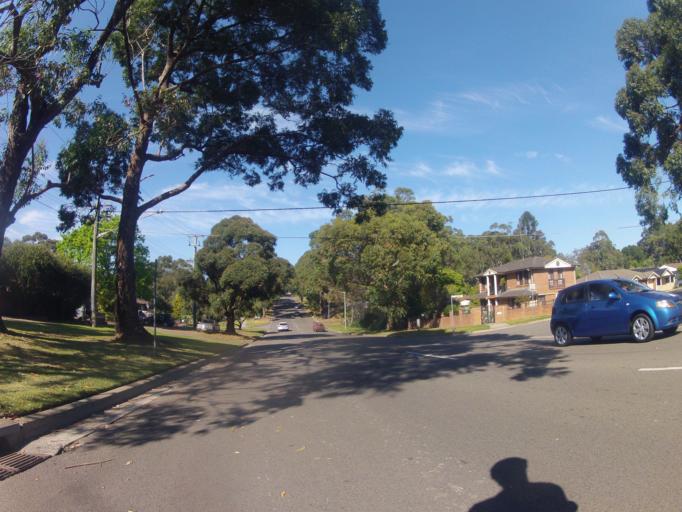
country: AU
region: New South Wales
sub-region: Sutherland Shire
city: Gymea
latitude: -34.0357
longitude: 151.0919
